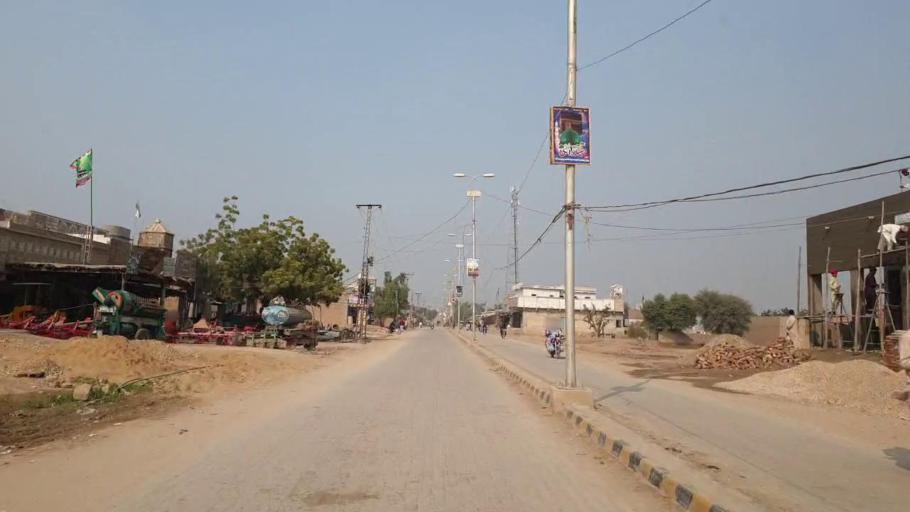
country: PK
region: Sindh
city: Bhan
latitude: 26.5498
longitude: 67.7184
